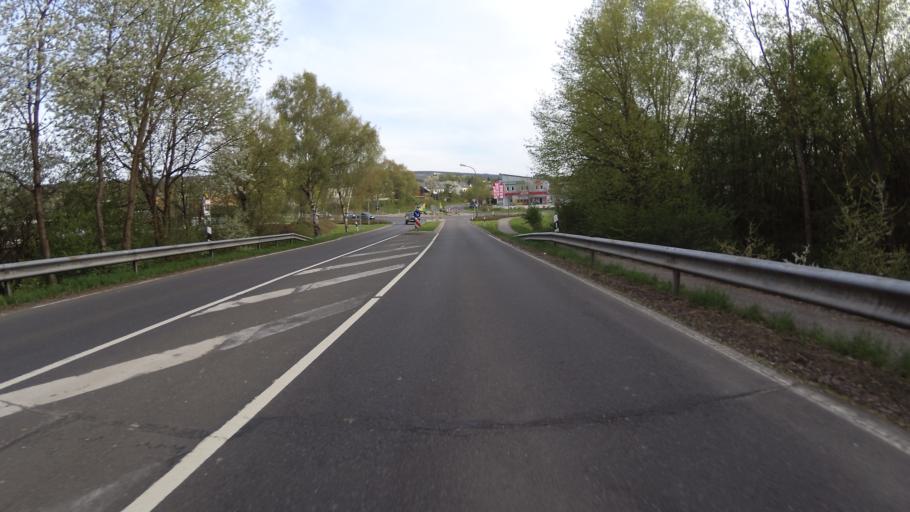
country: DE
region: Rheinland-Pfalz
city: Morbach
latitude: 49.8152
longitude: 7.1236
